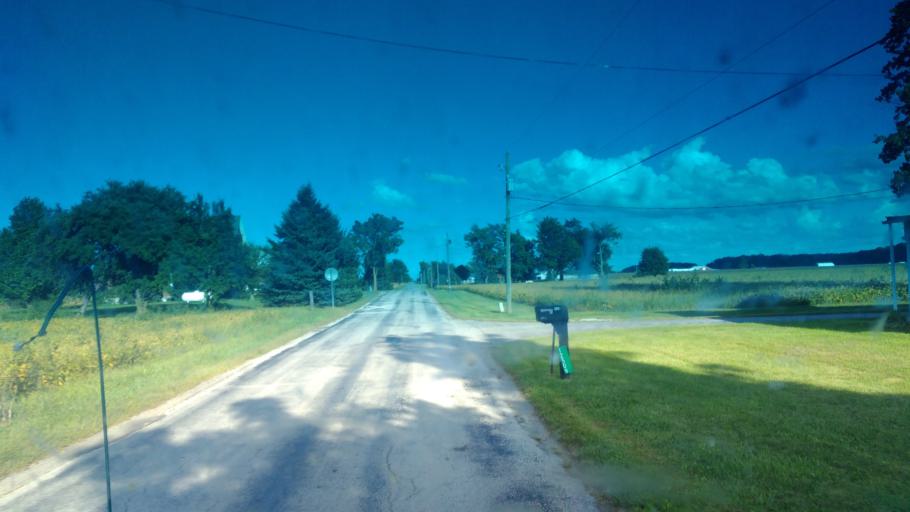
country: US
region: Ohio
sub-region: Hancock County
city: Arlington
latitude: 40.9357
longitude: -83.6410
